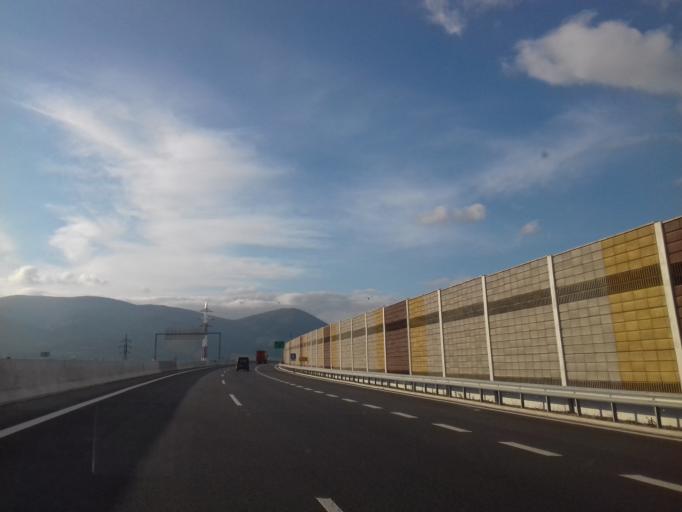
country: SK
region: Zilinsky
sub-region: Okres Zilina
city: Vrutky
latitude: 49.1098
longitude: 18.9526
